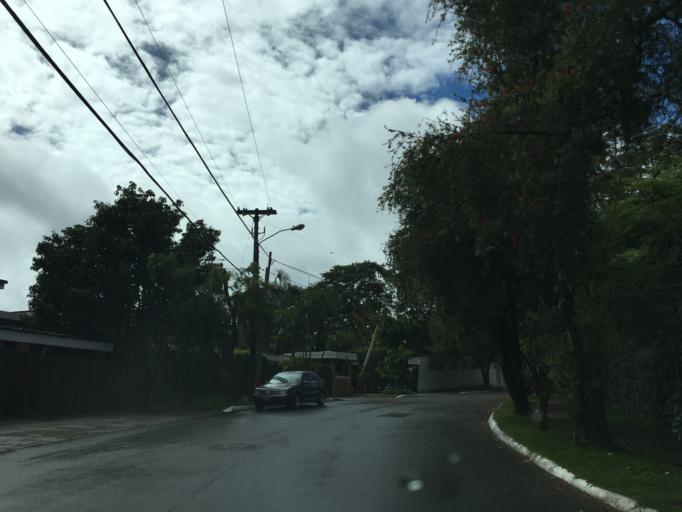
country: GT
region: Guatemala
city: Santa Catarina Pinula
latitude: 14.5823
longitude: -90.4891
